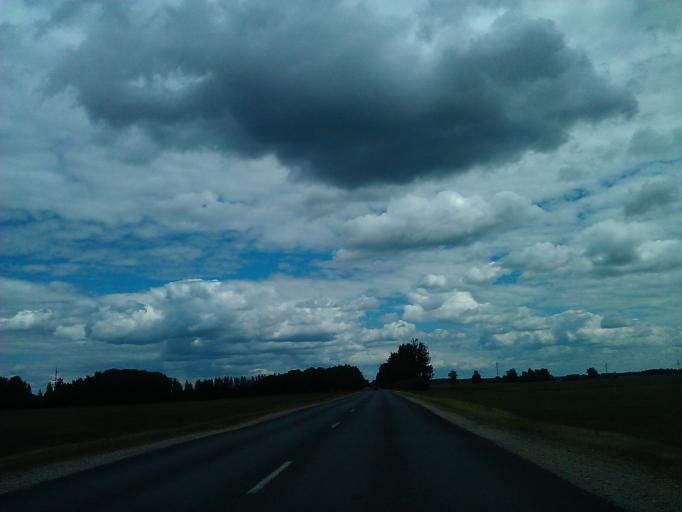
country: LV
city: Tervete
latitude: 56.6219
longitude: 23.4880
